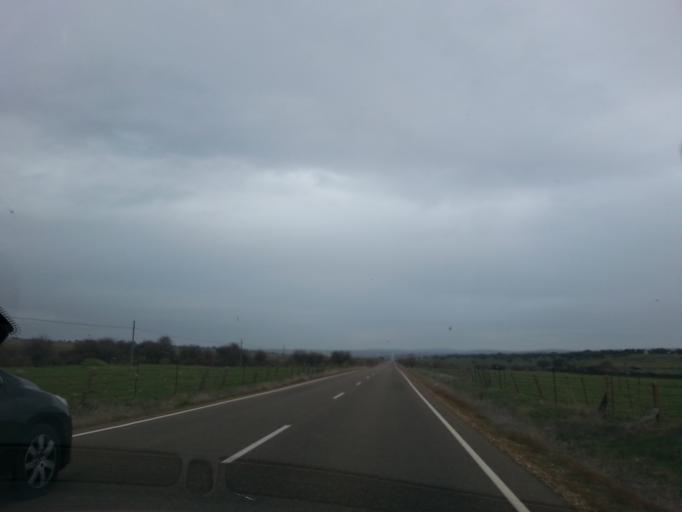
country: ES
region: Castille and Leon
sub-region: Provincia de Salamanca
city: Tamames
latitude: 40.6639
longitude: -6.0858
